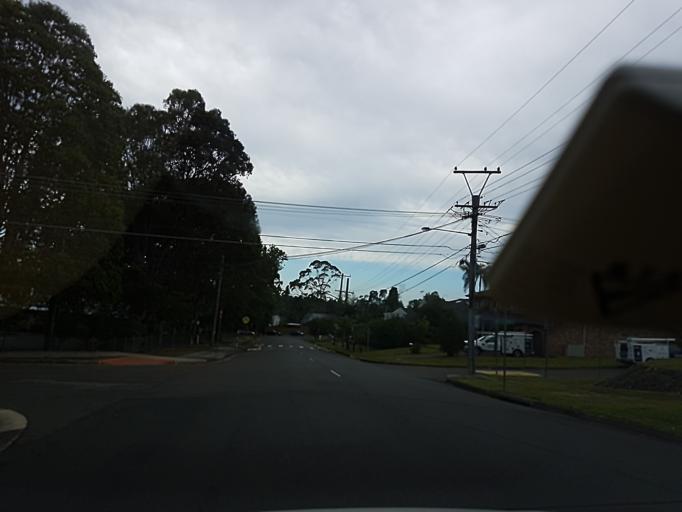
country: AU
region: New South Wales
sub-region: Warringah
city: Davidson
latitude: -33.7269
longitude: 151.2149
